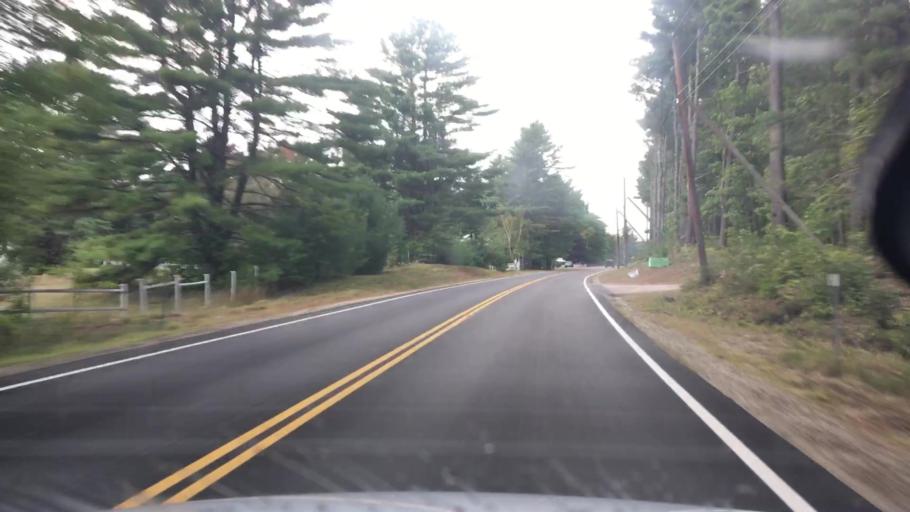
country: US
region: New Hampshire
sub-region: Carroll County
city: Sanbornville
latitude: 43.5348
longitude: -71.0249
